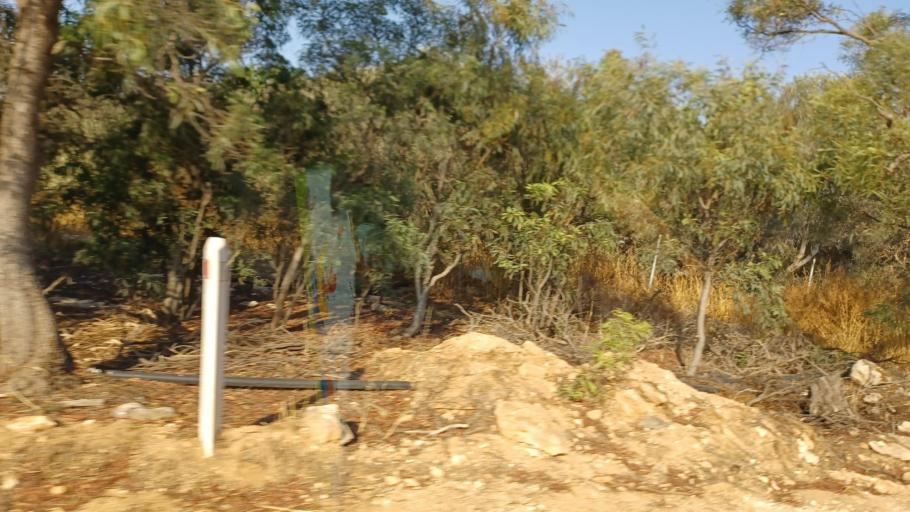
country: CY
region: Ammochostos
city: Frenaros
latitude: 35.0526
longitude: 33.9152
